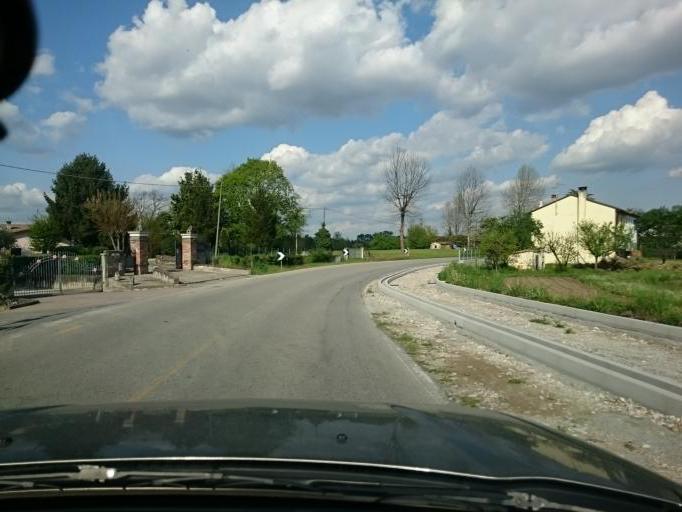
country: IT
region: Veneto
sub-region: Provincia di Padova
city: Trebaseleghe
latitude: 45.5794
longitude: 12.0214
